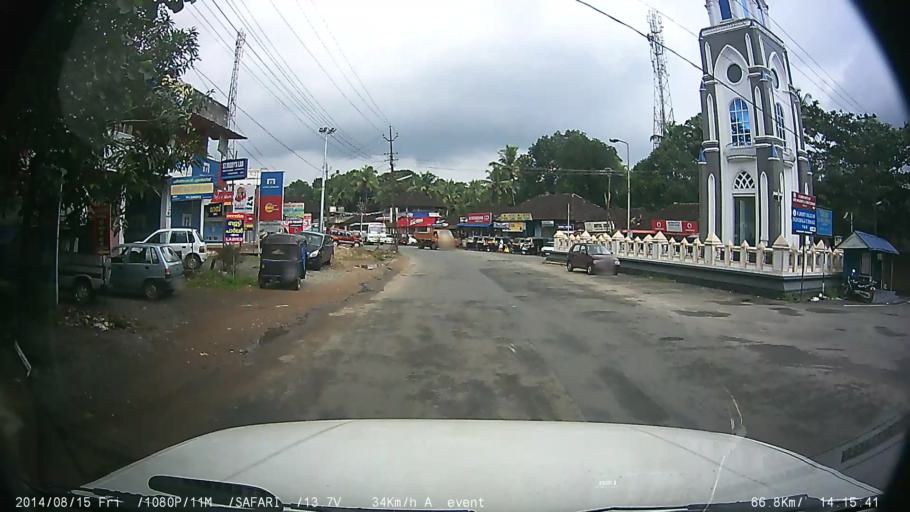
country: IN
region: Kerala
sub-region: Kottayam
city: Lalam
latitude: 9.7452
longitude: 76.7023
